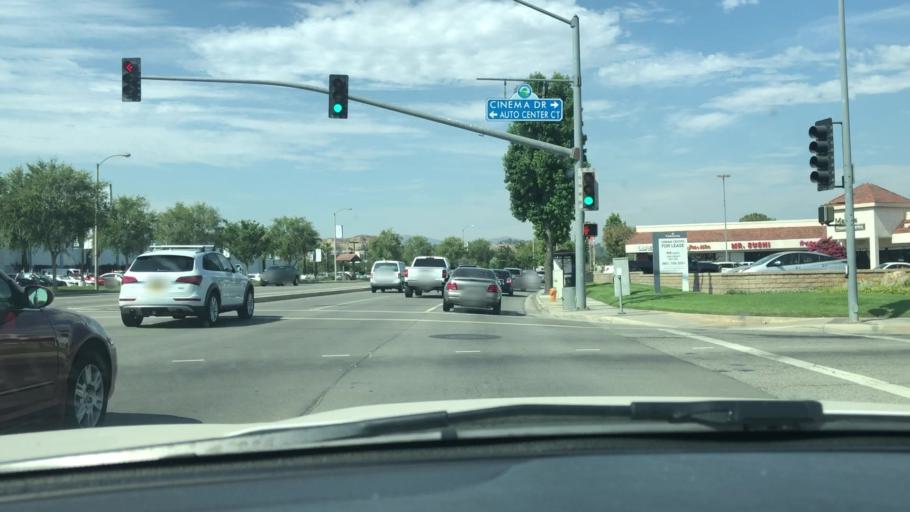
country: US
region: California
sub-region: Los Angeles County
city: Santa Clarita
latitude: 34.4210
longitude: -118.5476
